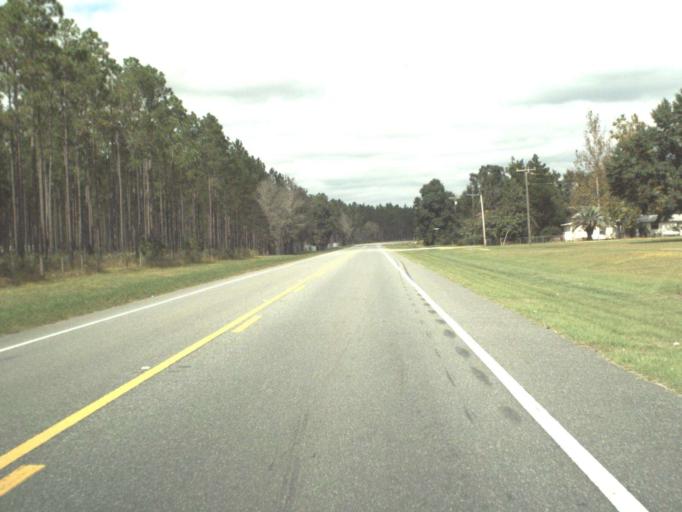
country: US
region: Florida
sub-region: Calhoun County
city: Blountstown
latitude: 30.5065
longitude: -85.2002
